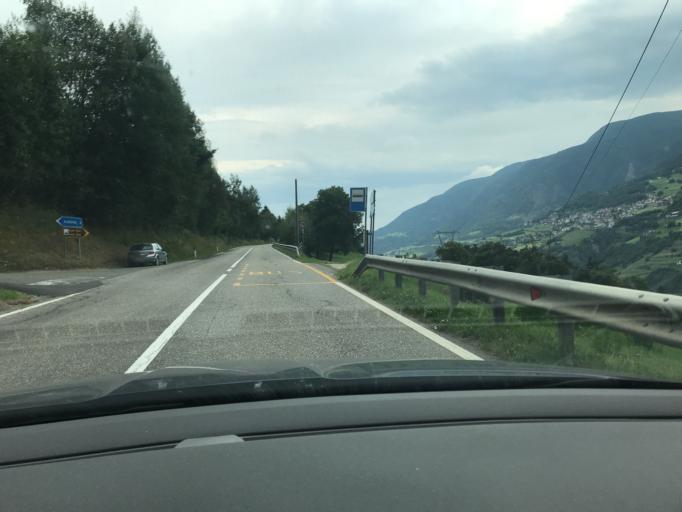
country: IT
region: Trentino-Alto Adige
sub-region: Bolzano
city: Villandro
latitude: 46.6172
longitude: 11.5475
